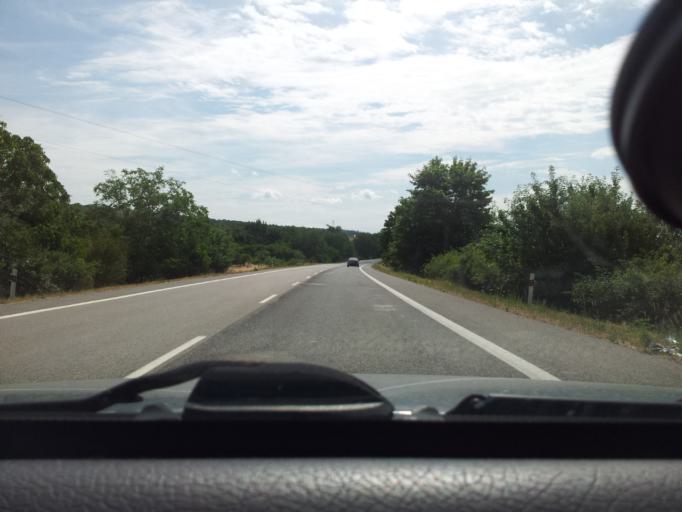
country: SK
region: Nitriansky
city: Zlate Moravce
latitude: 48.3713
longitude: 18.4363
